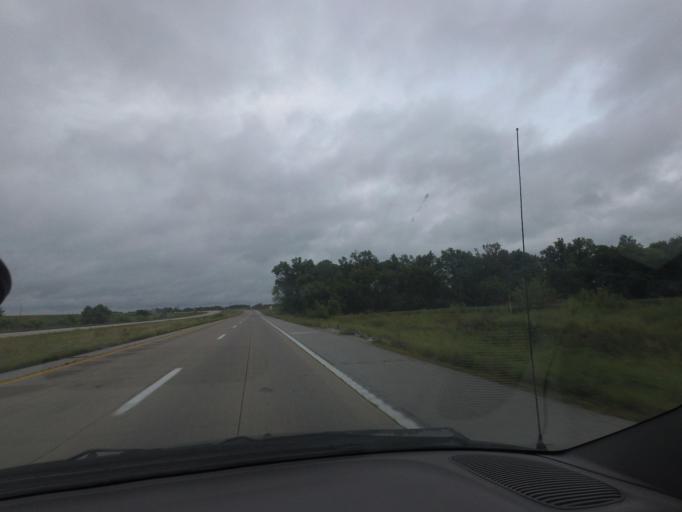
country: US
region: Missouri
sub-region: Marion County
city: Monroe City
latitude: 39.6671
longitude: -91.8510
